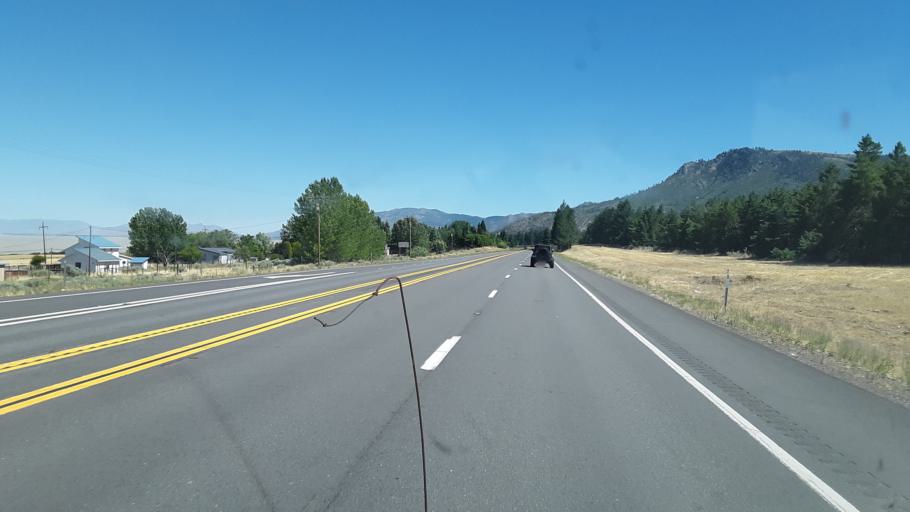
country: US
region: California
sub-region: Lassen County
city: Janesville
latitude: 40.2543
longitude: -120.4649
